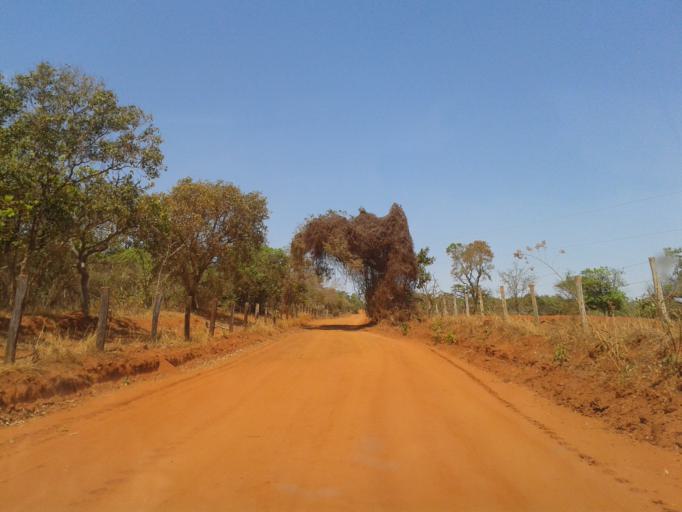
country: BR
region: Minas Gerais
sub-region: Ituiutaba
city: Ituiutaba
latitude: -19.0711
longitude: -49.3186
